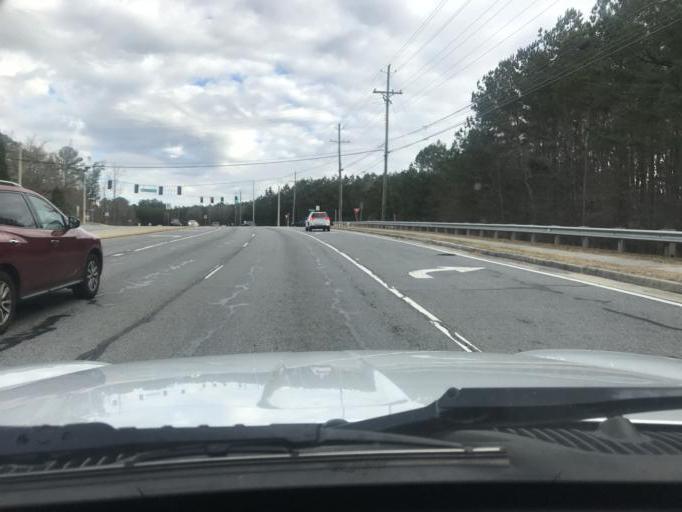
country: US
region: Georgia
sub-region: Gwinnett County
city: Buford
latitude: 34.0694
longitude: -83.9716
